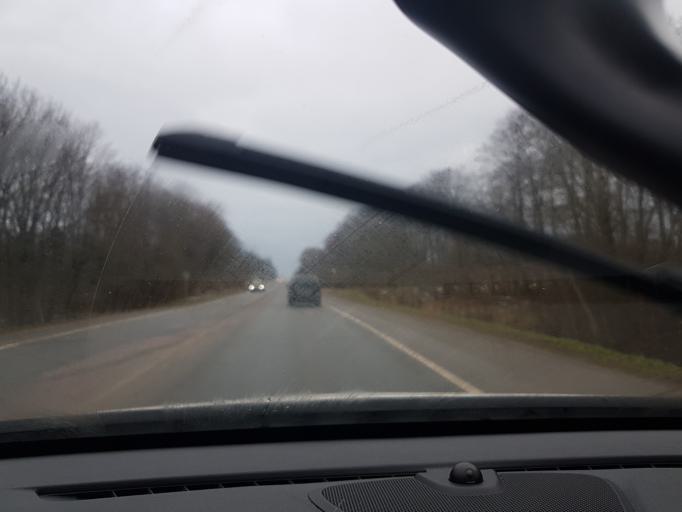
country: RU
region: Moskovskaya
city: Sychevo
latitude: 56.0077
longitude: 36.2330
